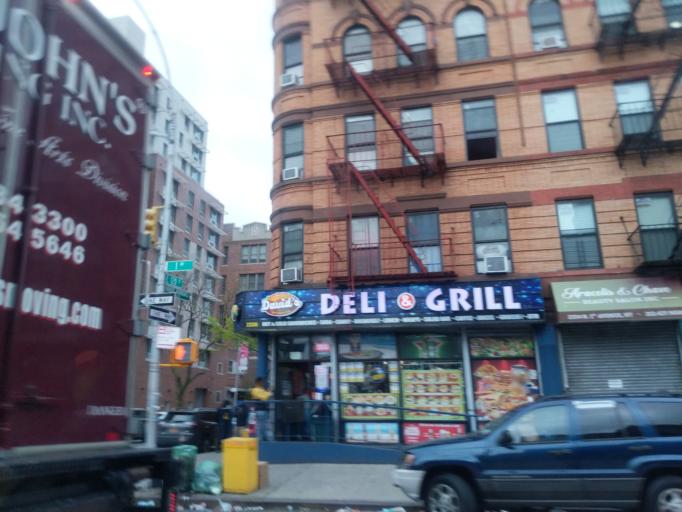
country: US
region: New York
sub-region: New York County
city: Manhattan
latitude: 40.7984
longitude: -73.9336
